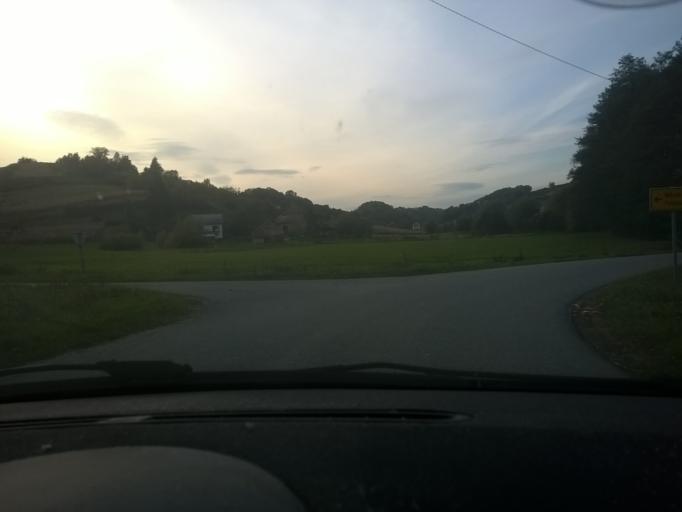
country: HR
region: Krapinsko-Zagorska
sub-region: Grad Krapina
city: Krapina
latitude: 46.1231
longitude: 15.8517
